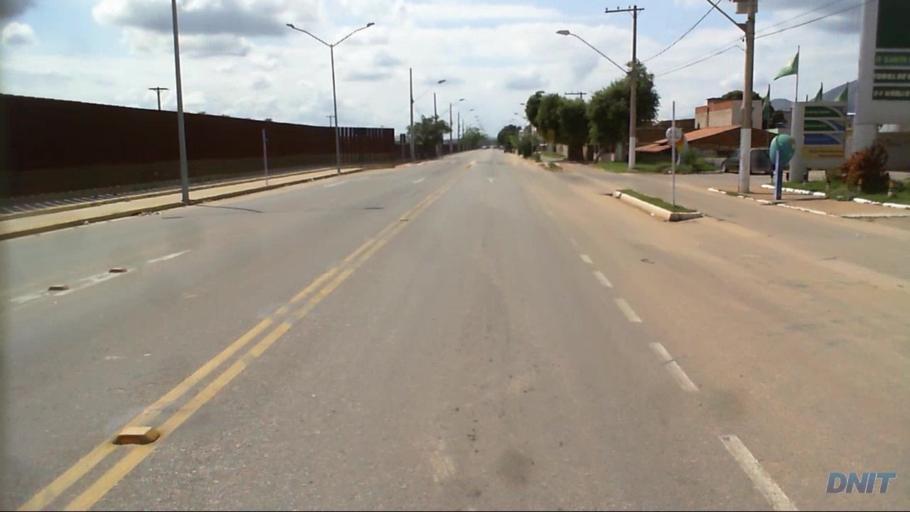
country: BR
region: Minas Gerais
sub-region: Governador Valadares
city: Governador Valadares
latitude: -18.9034
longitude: -41.9883
